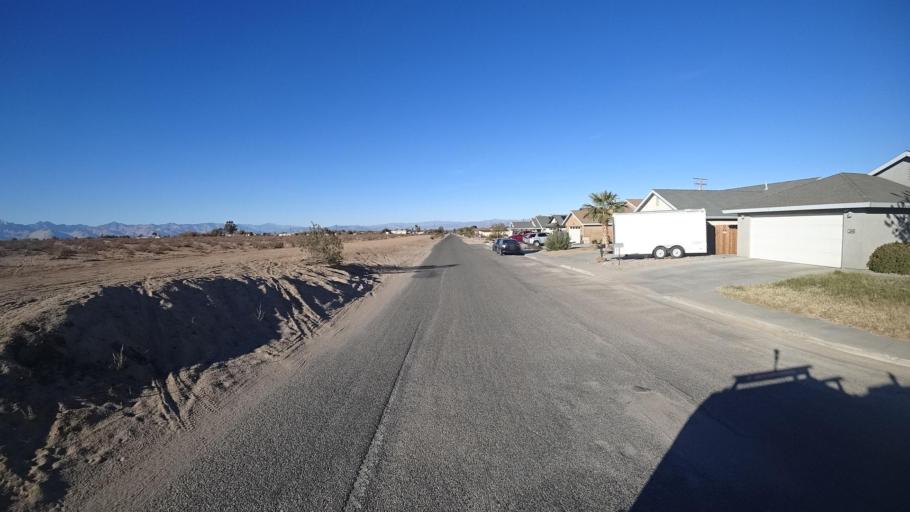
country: US
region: California
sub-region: Kern County
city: Ridgecrest
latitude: 35.5935
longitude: -117.6972
